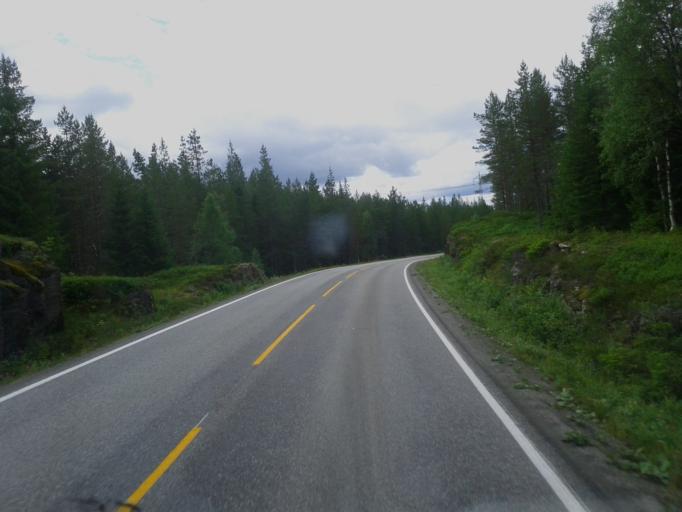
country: NO
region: Nord-Trondelag
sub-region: Hoylandet
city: Hoylandet
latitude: 64.6539
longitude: 12.6495
